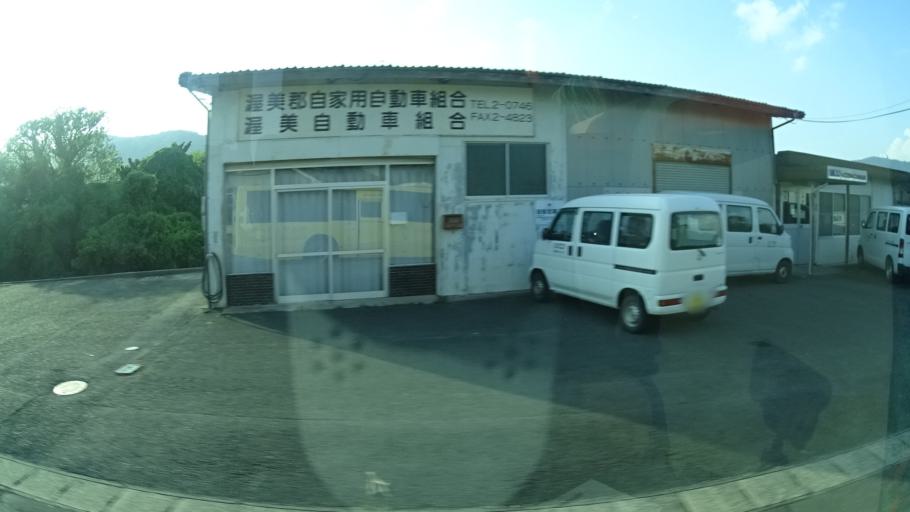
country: JP
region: Aichi
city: Tahara
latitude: 34.6618
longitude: 137.2551
